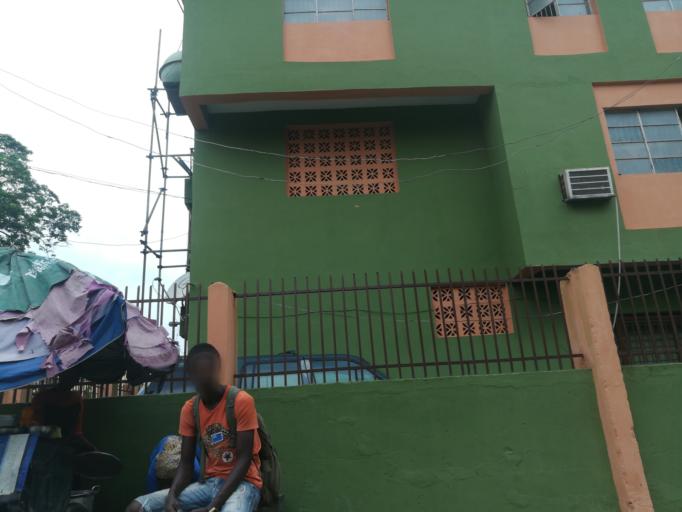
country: NG
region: Lagos
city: Ebute Metta
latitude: 6.4856
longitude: 3.3836
